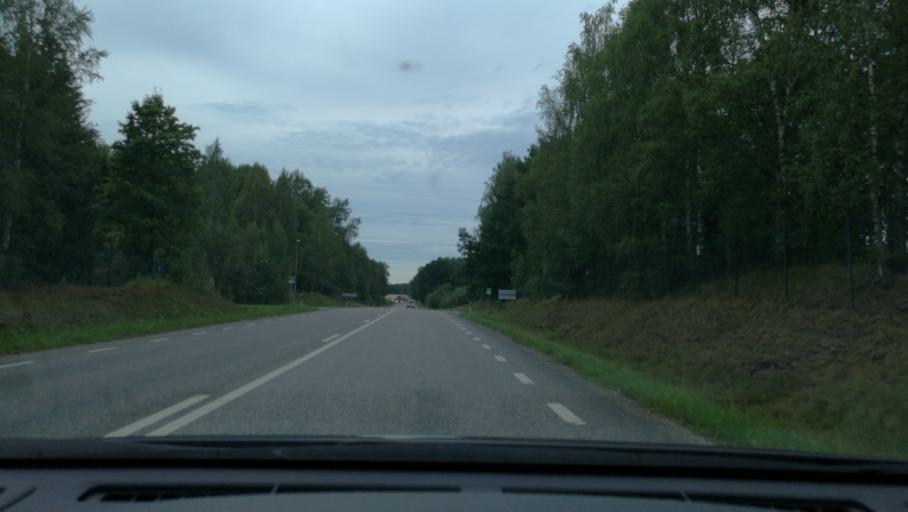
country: SE
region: Soedermanland
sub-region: Katrineholms Kommun
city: Katrineholm
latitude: 59.0122
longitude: 16.2134
